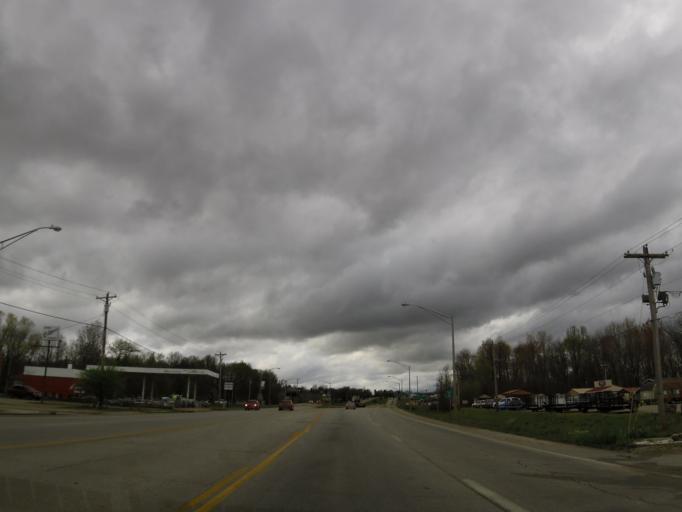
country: US
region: Missouri
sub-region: Butler County
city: Poplar Bluff
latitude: 36.7460
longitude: -90.4121
